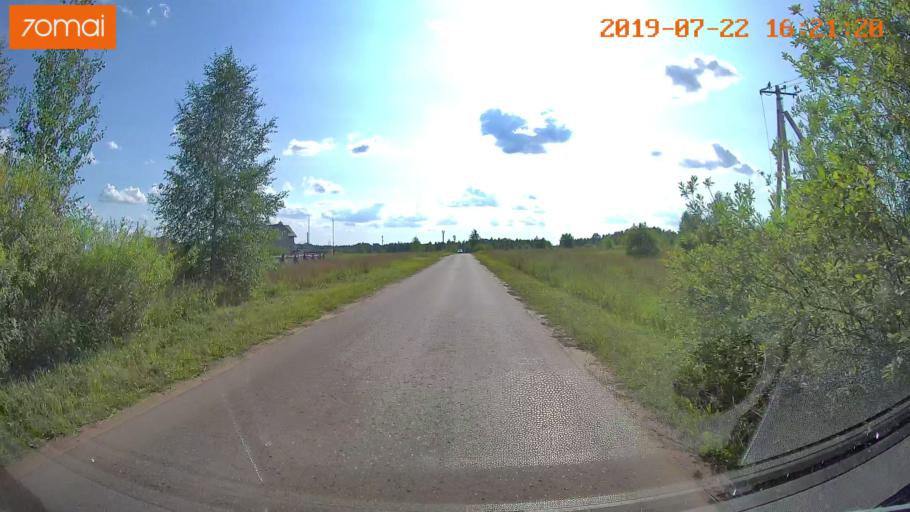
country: RU
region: Ivanovo
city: Novo-Talitsy
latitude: 57.0625
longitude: 40.8881
